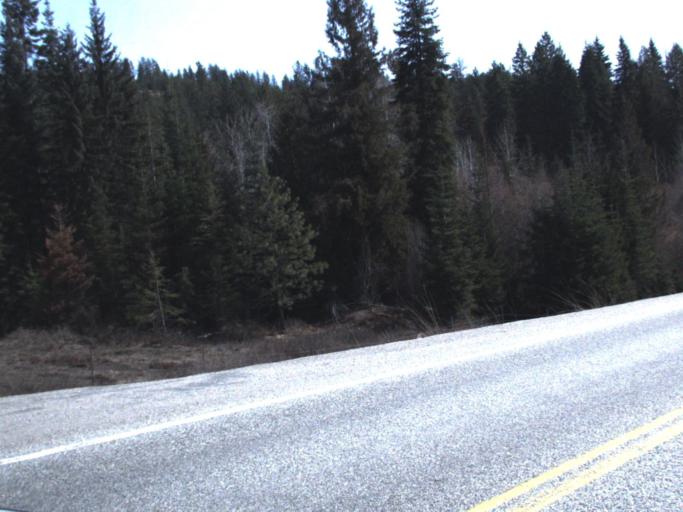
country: US
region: Washington
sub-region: Stevens County
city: Colville
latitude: 48.5158
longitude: -117.7545
